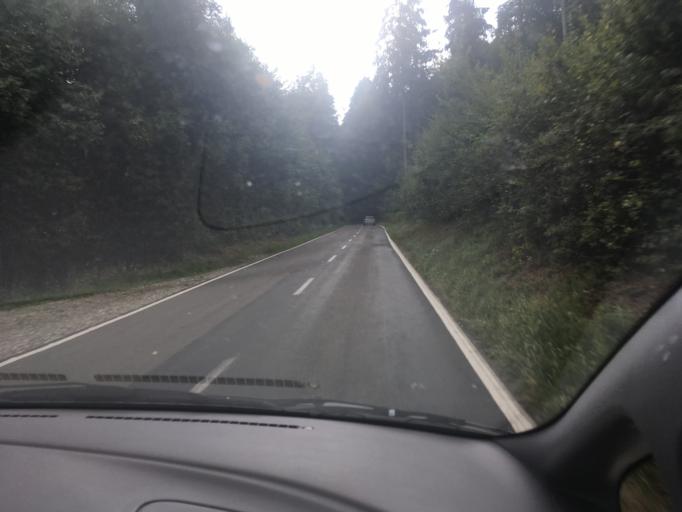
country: CH
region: Bern
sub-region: Bern-Mittelland District
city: Wohlen
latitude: 47.0063
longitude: 7.3507
